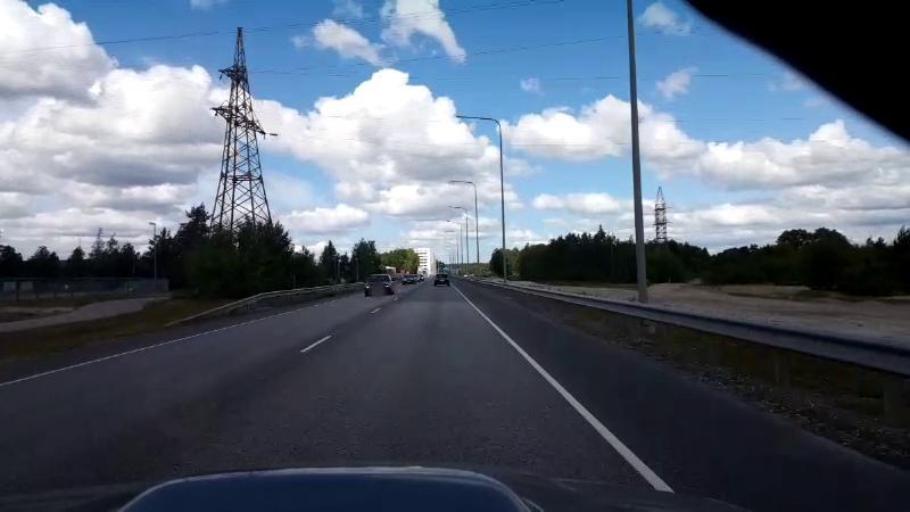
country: EE
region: Paernumaa
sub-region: Paernu linn
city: Parnu
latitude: 58.3712
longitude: 24.5559
